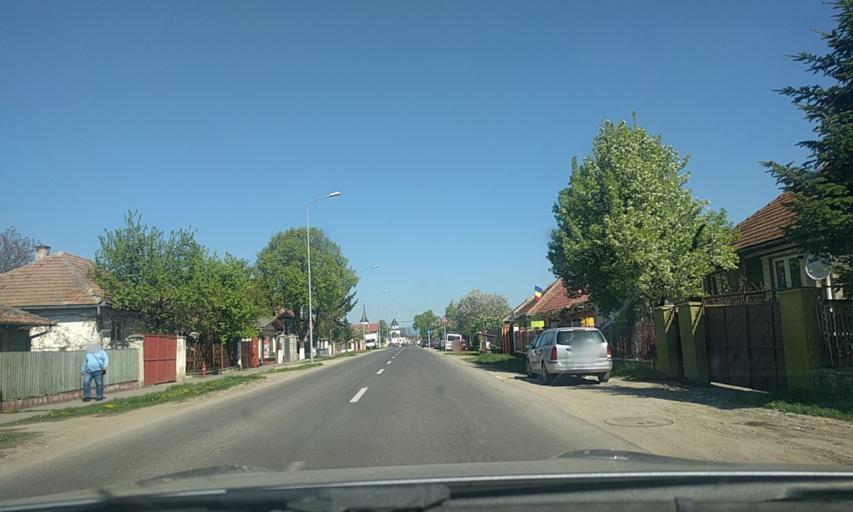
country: RO
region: Brasov
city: Brasov
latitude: 45.6955
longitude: 25.5606
